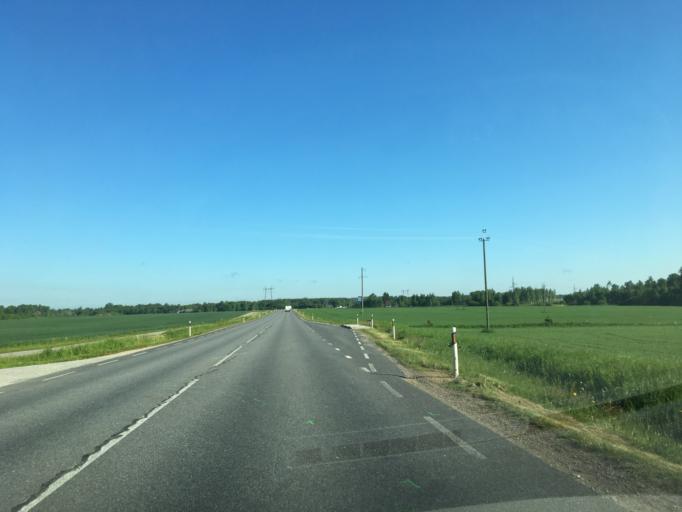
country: EE
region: Tartu
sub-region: Tartu linn
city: Tartu
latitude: 58.4456
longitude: 26.6792
